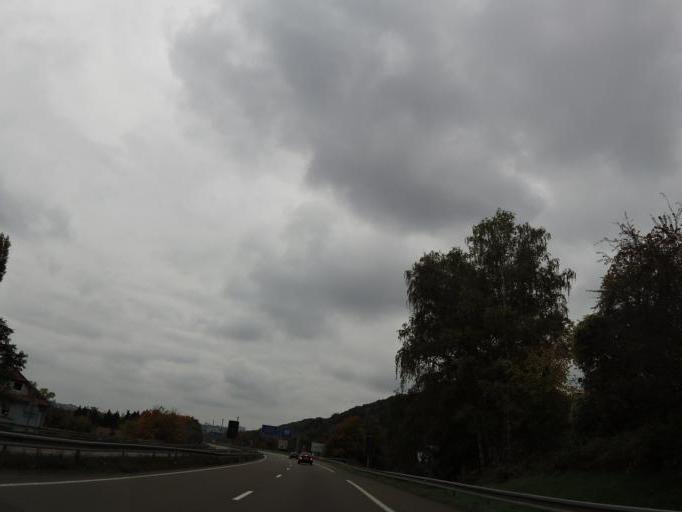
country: FR
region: Lorraine
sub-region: Departement de la Moselle
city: Spicheren
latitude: 49.2030
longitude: 6.9568
